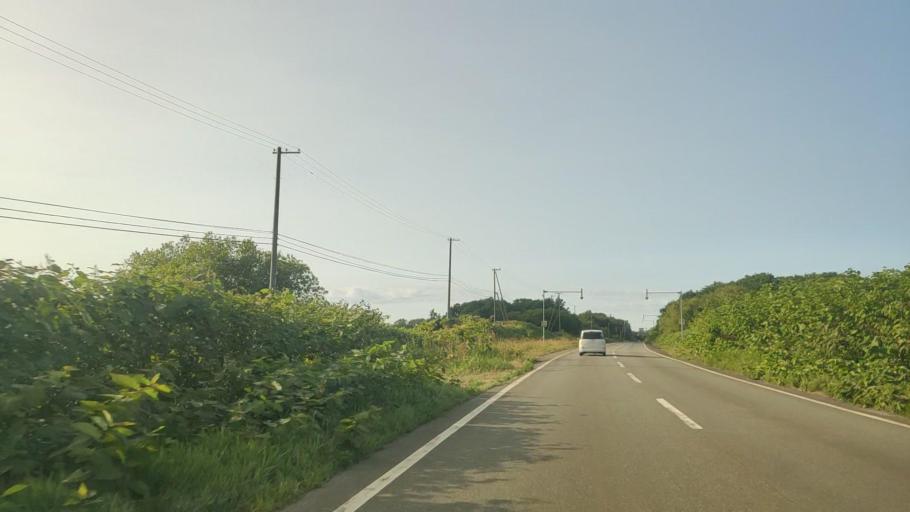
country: JP
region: Hokkaido
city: Makubetsu
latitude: 45.0578
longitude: 141.7486
